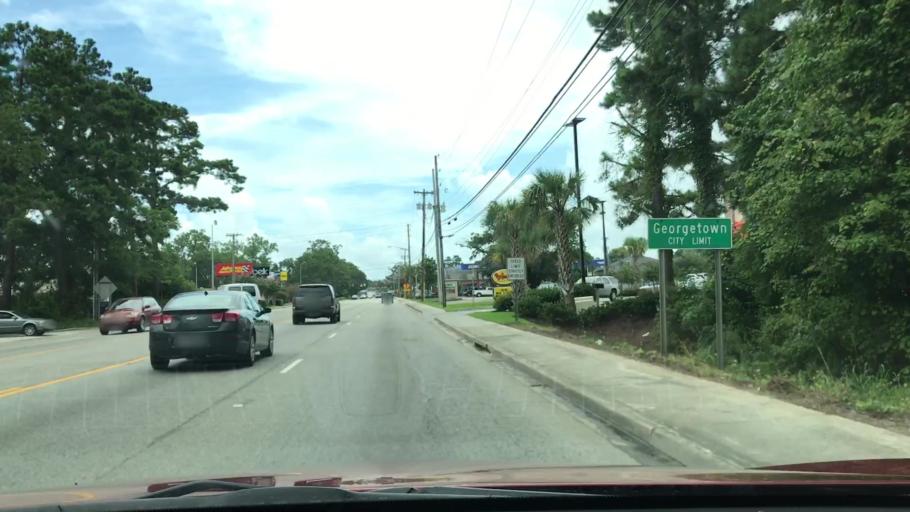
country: US
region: South Carolina
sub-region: Georgetown County
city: Georgetown
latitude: 33.3930
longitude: -79.2892
